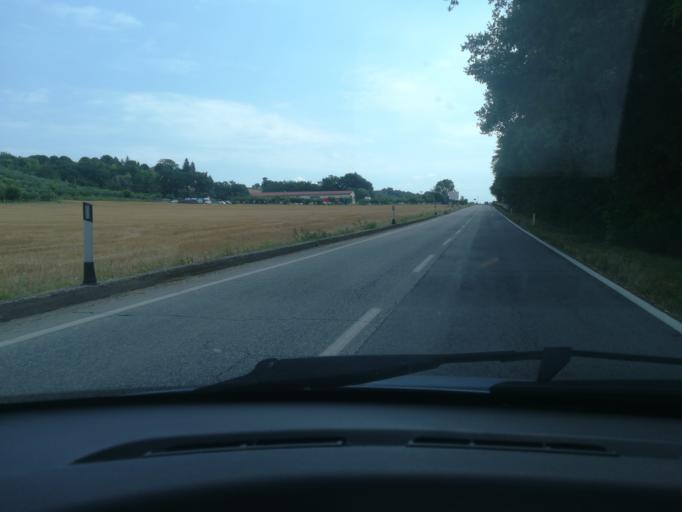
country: IT
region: The Marches
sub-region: Provincia di Macerata
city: Sforzacosta
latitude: 43.2617
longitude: 13.4362
